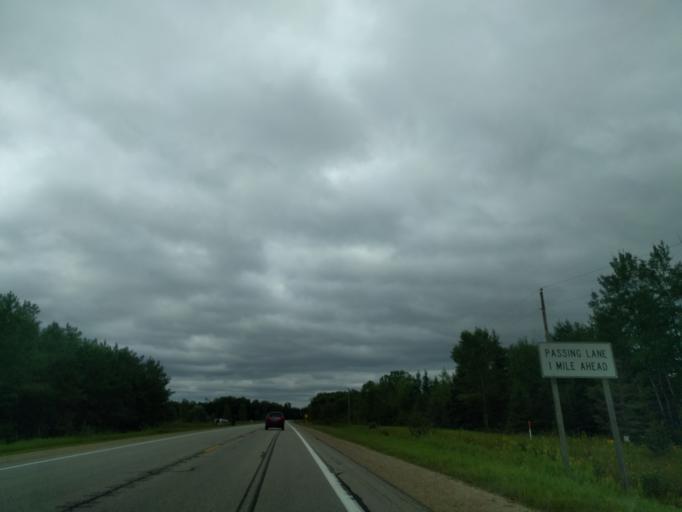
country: US
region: Michigan
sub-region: Delta County
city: Escanaba
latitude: 45.5633
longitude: -87.2596
